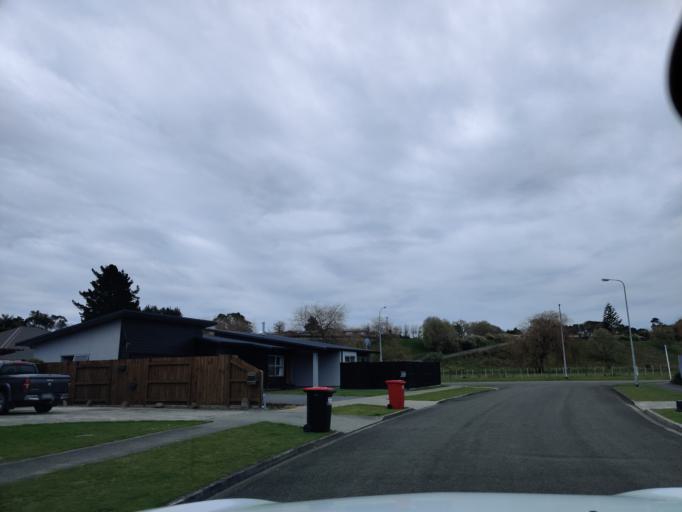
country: NZ
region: Manawatu-Wanganui
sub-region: Palmerston North City
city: Palmerston North
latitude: -40.2853
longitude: 175.7493
